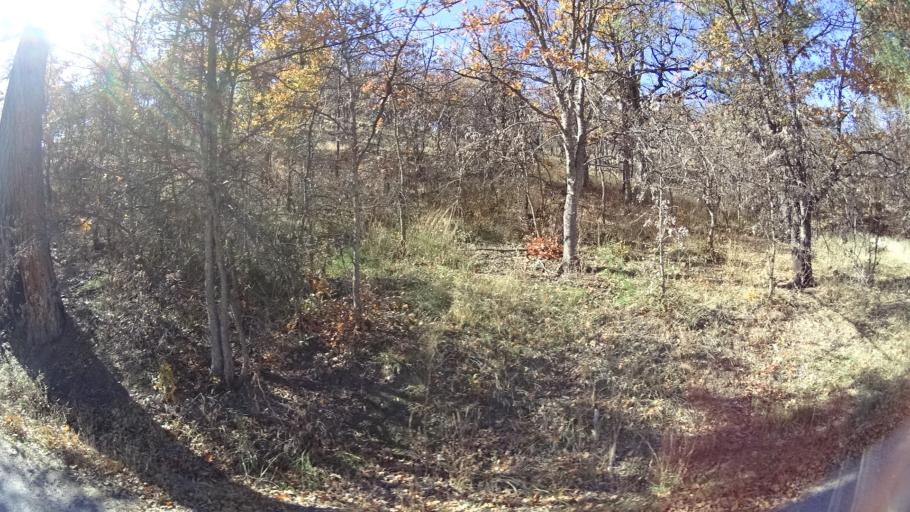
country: US
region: California
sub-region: Siskiyou County
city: Yreka
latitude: 41.9416
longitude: -122.5917
